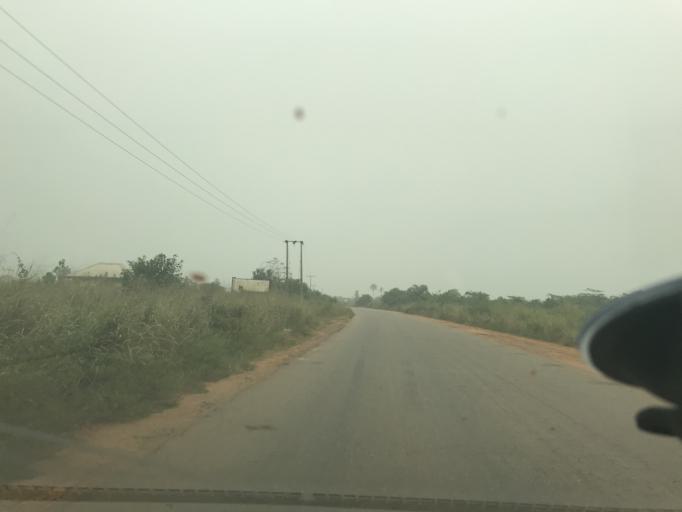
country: NG
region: Ogun
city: Owode
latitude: 6.8871
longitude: 3.5290
